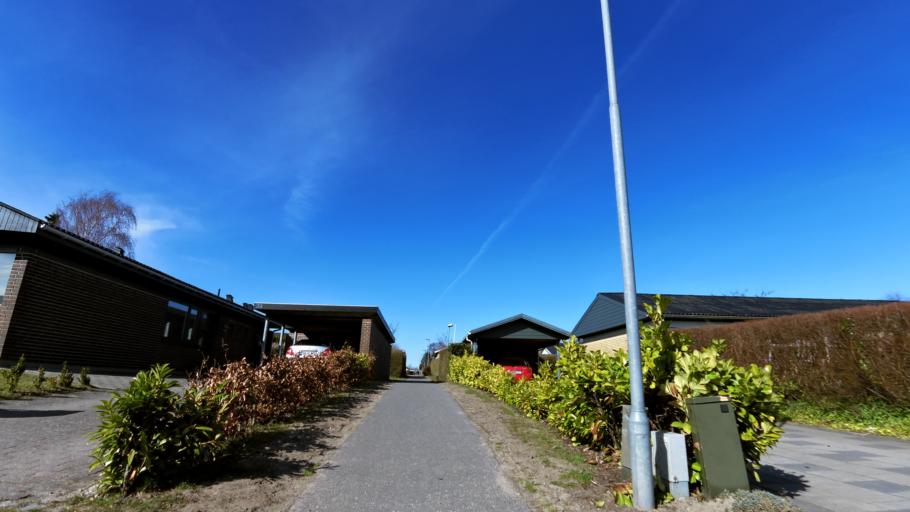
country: DK
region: Central Jutland
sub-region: Arhus Kommune
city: Stavtrup
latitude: 56.1768
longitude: 10.1103
